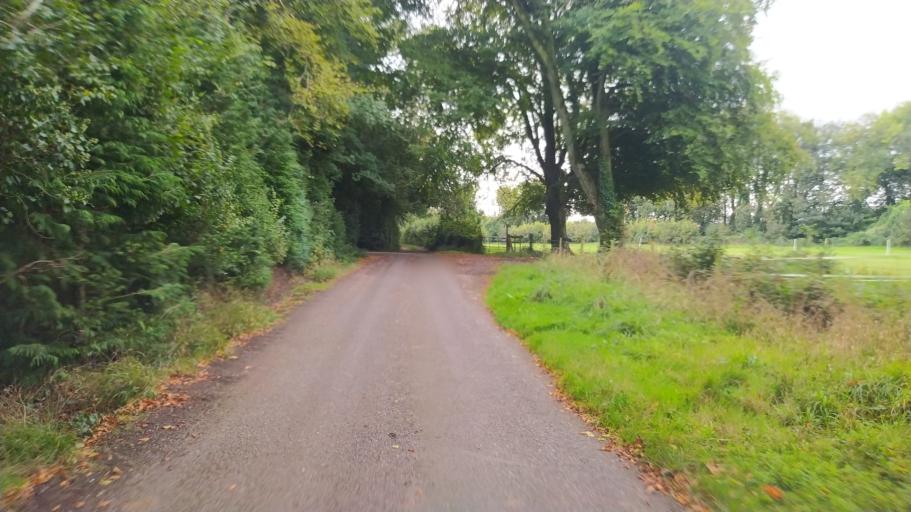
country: GB
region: England
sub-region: Dorset
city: Blandford Forum
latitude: 50.8131
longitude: -2.1989
